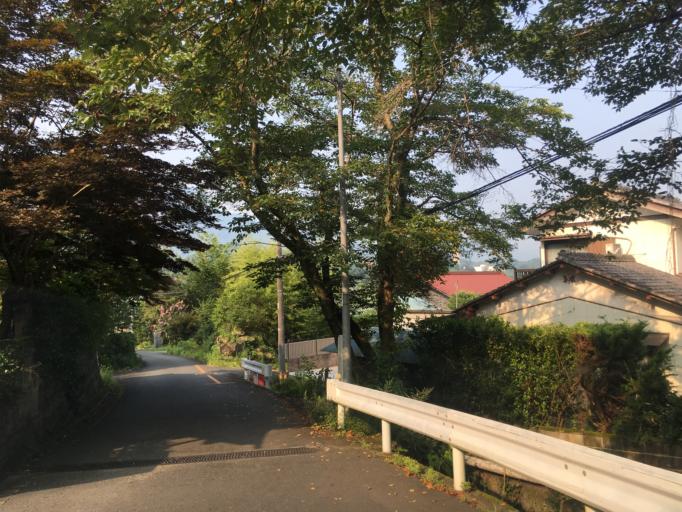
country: JP
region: Saitama
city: Chichibu
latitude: 35.9860
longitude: 139.1124
